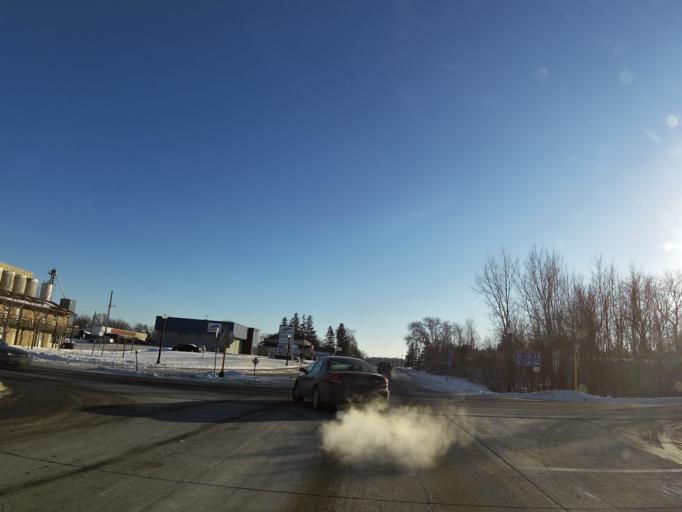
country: US
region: Minnesota
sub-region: Le Sueur County
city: New Prague
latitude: 44.5439
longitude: -93.5842
